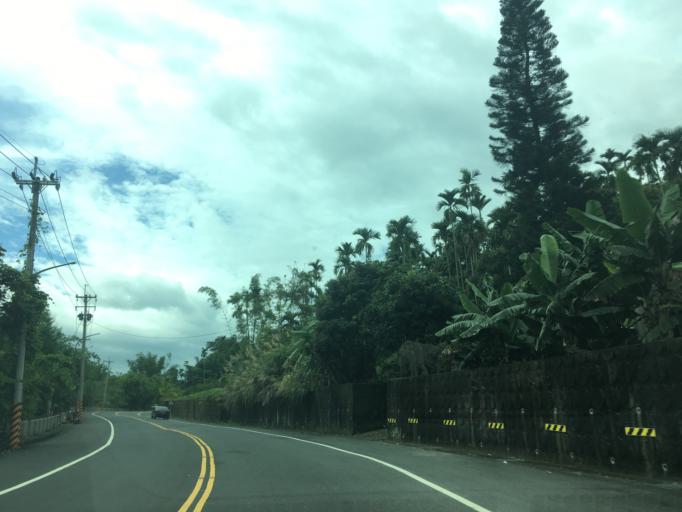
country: TW
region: Taiwan
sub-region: Yunlin
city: Douliu
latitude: 23.5740
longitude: 120.5641
